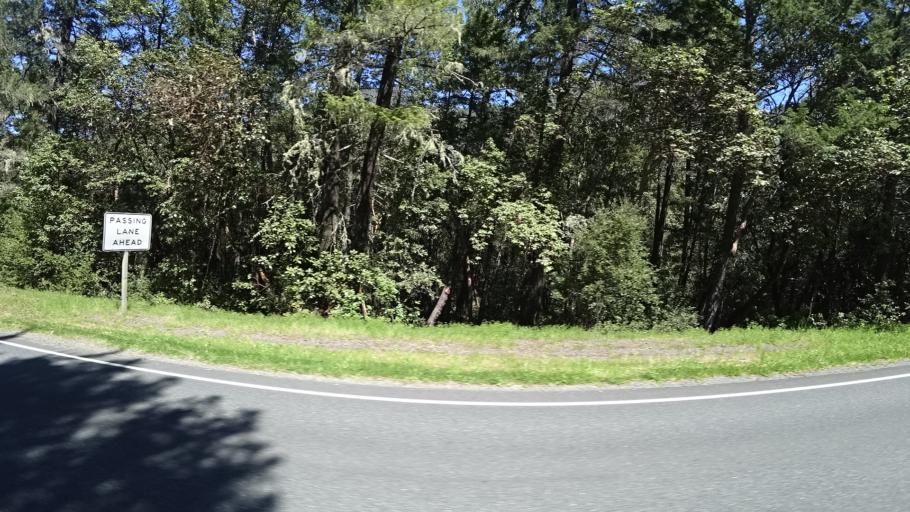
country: US
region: California
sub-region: Humboldt County
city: Willow Creek
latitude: 40.8544
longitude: -123.4920
